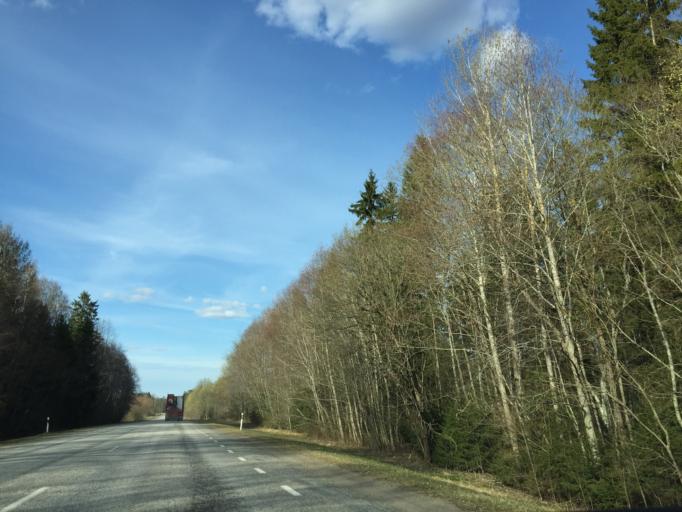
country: EE
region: Tartu
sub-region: Elva linn
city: Elva
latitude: 58.1194
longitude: 26.5155
